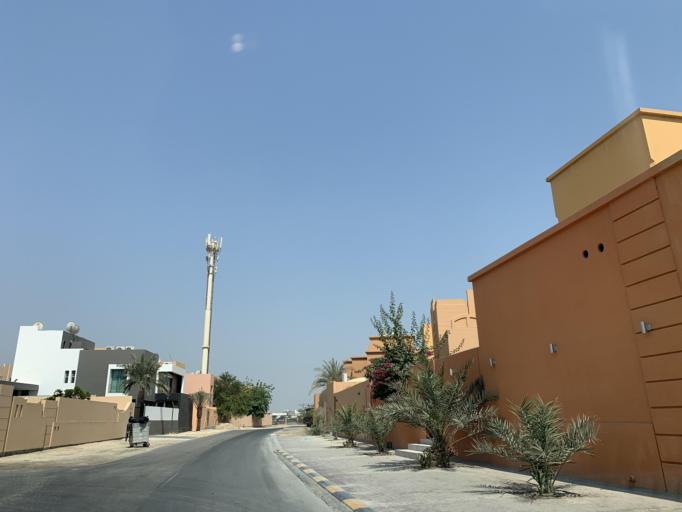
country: BH
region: Manama
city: Jidd Hafs
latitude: 26.2101
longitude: 50.5227
